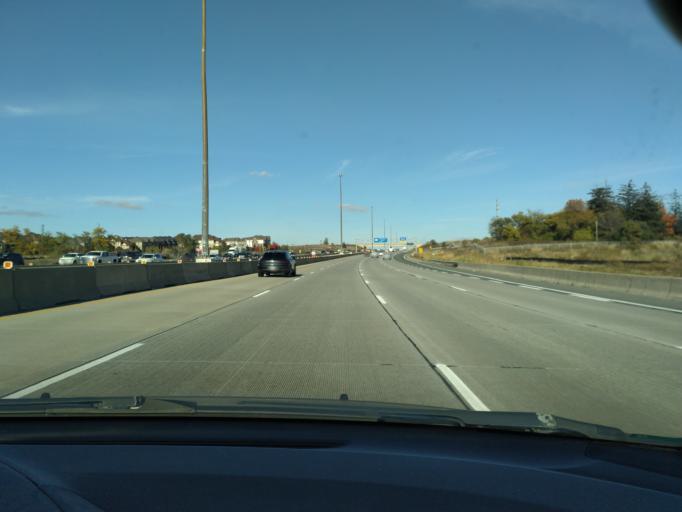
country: CA
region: Ontario
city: Brampton
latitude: 43.6358
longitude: -79.7432
